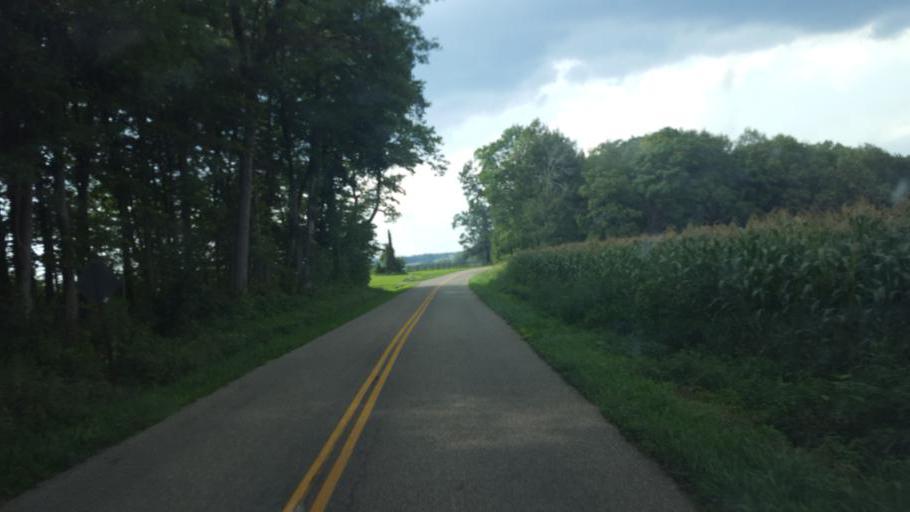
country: US
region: Ohio
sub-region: Knox County
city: Gambier
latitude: 40.3385
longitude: -82.3513
